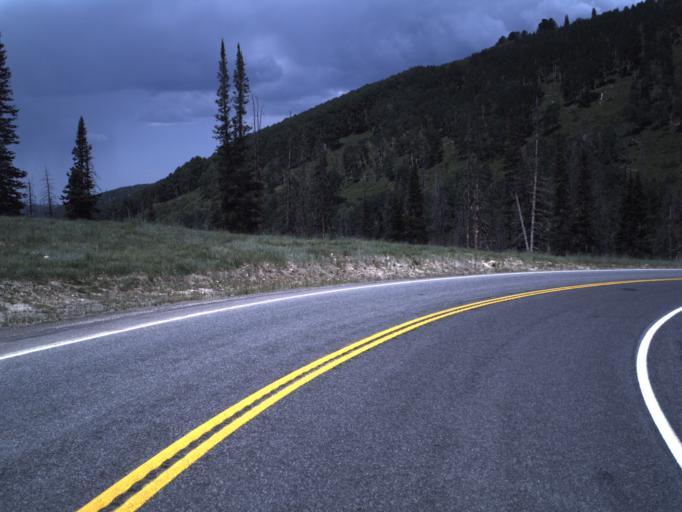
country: US
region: Utah
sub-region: Sanpete County
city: Fairview
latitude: 39.6803
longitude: -111.2312
